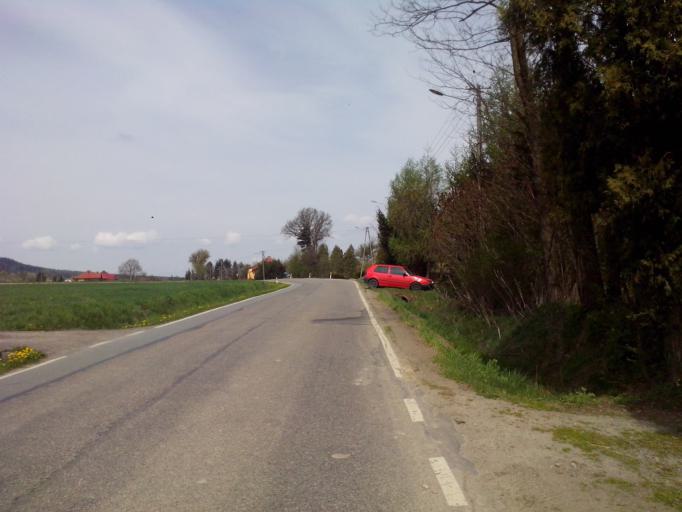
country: PL
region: Subcarpathian Voivodeship
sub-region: Powiat strzyzowski
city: Jawornik
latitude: 49.8069
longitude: 21.8555
